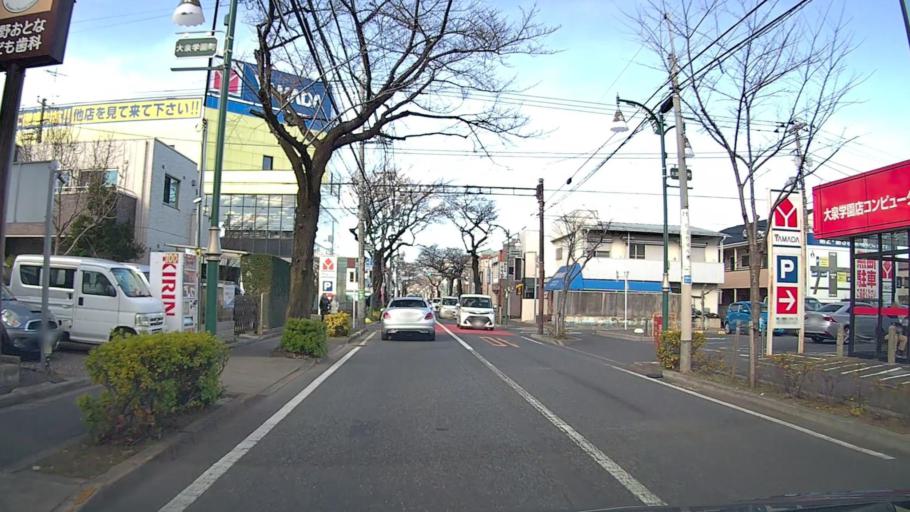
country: JP
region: Saitama
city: Asaka
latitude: 35.7682
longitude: 139.5872
